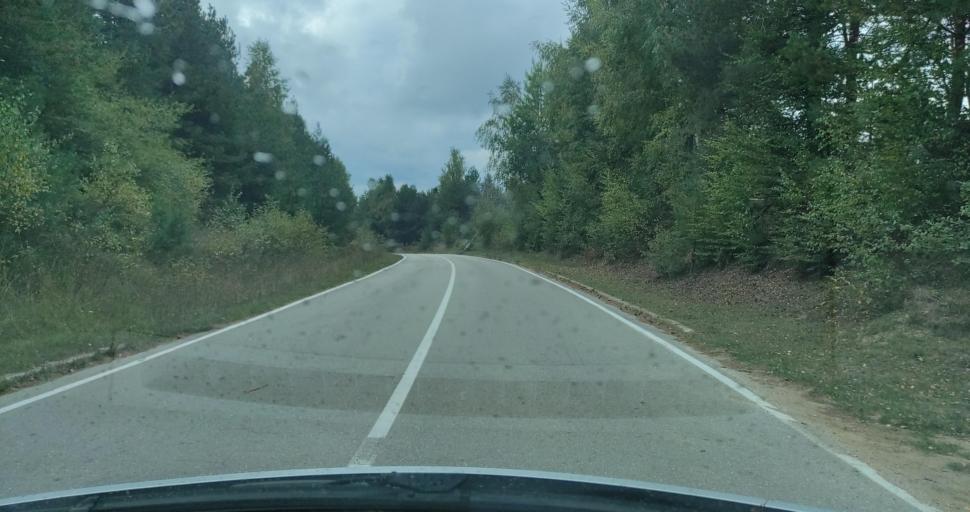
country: RS
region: Central Serbia
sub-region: Jablanicki Okrug
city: Crna Trava
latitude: 42.6801
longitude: 22.3123
